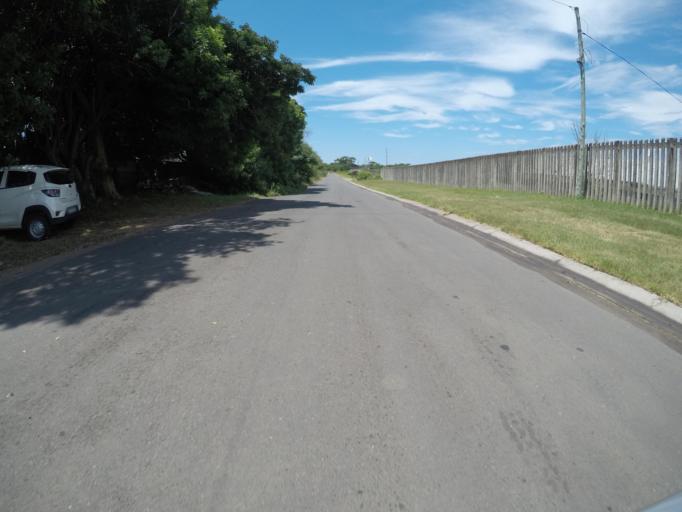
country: ZA
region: Eastern Cape
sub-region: Buffalo City Metropolitan Municipality
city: East London
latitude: -33.0364
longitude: 27.8439
